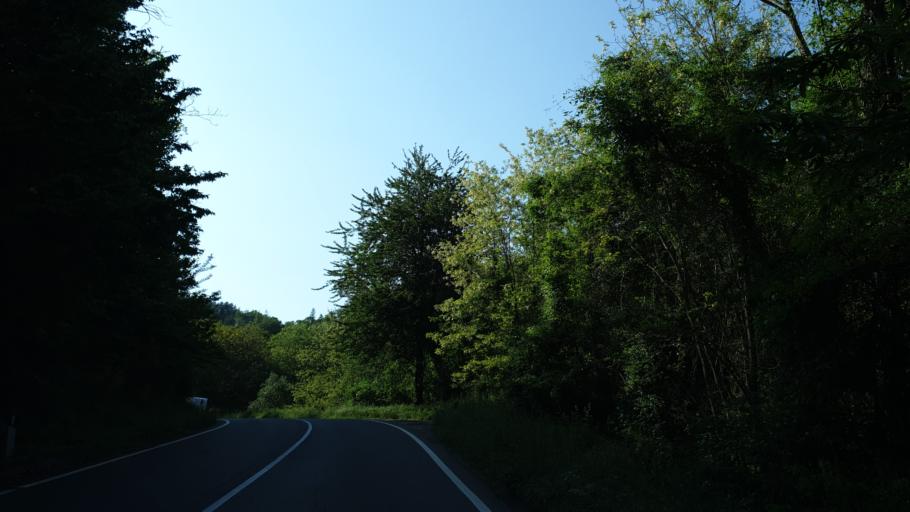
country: IT
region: Tuscany
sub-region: Province of Arezzo
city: Stia
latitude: 43.7737
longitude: 11.6952
